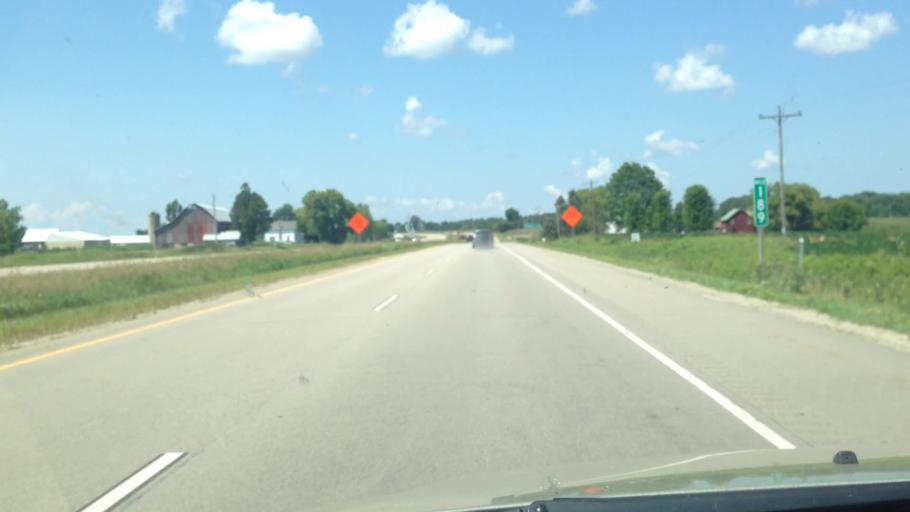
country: US
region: Wisconsin
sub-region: Oconto County
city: Oconto Falls
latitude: 44.8006
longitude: -88.0104
